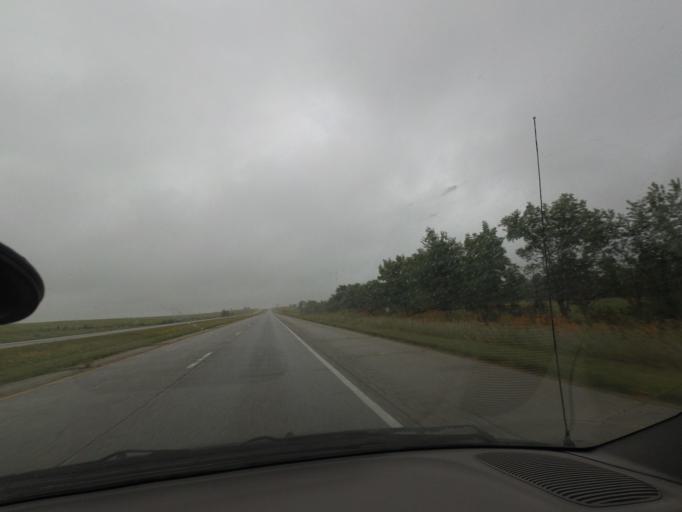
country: US
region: Illinois
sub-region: Pike County
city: Barry
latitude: 39.7025
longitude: -91.0324
